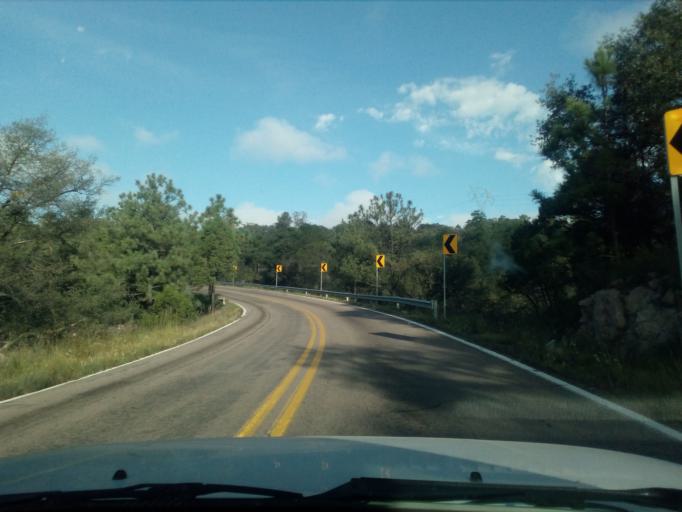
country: MX
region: Durango
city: Victoria de Durango
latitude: 23.9326
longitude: -104.9129
